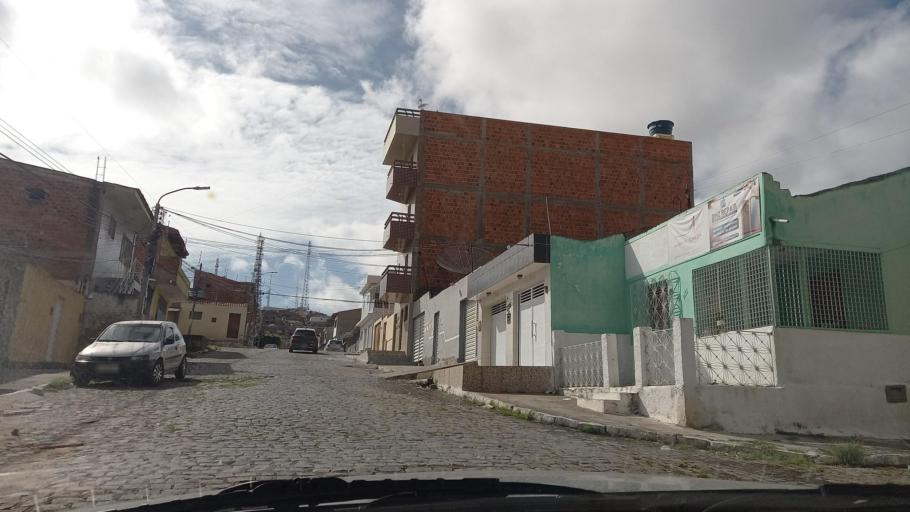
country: BR
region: Pernambuco
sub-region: Caruaru
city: Caruaru
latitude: -8.2853
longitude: -35.9825
